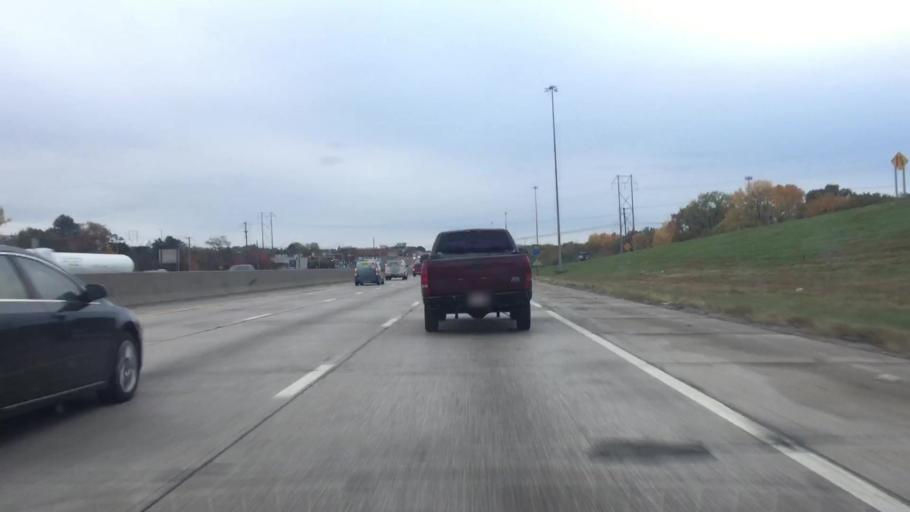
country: US
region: Kansas
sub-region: Johnson County
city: Overland Park
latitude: 38.9923
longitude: -94.6979
